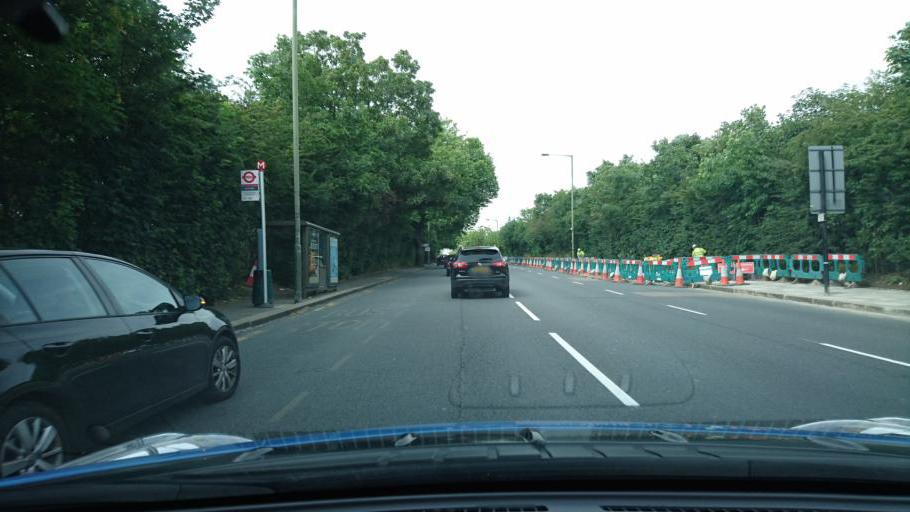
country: GB
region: England
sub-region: Greater London
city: Hendon
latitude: 51.6055
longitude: -0.1750
